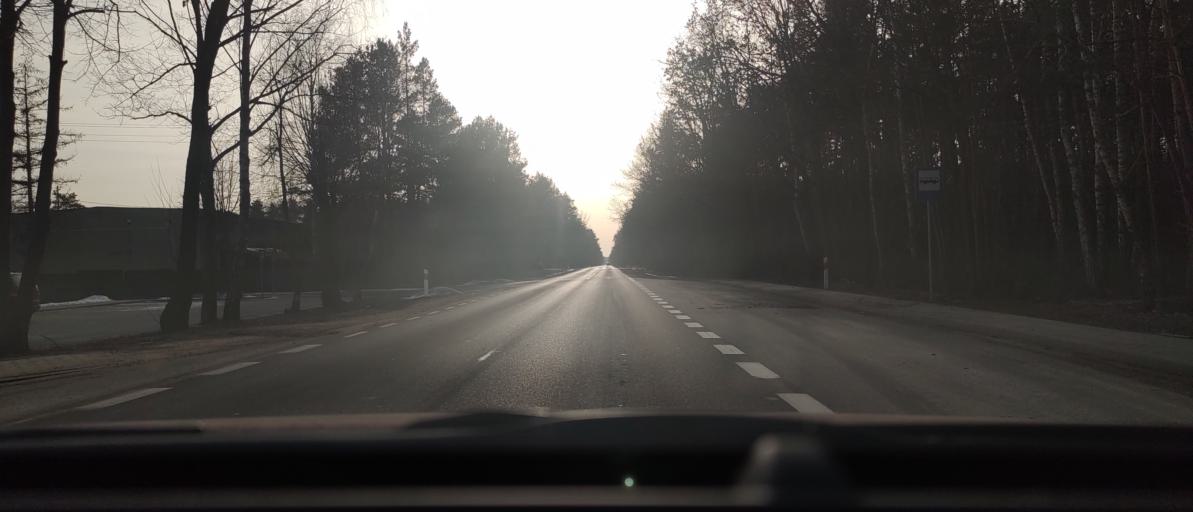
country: PL
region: Masovian Voivodeship
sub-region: Powiat bialobrzeski
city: Bialobrzegi
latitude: 51.6416
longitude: 20.9174
